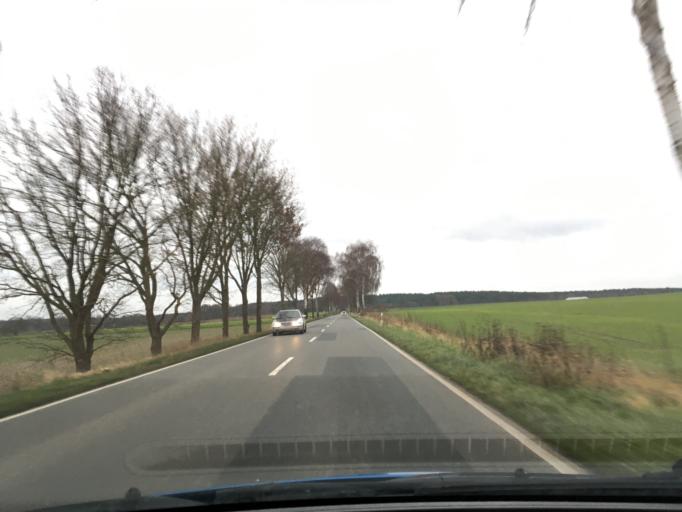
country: DE
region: Lower Saxony
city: Neetze
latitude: 53.2671
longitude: 10.6370
